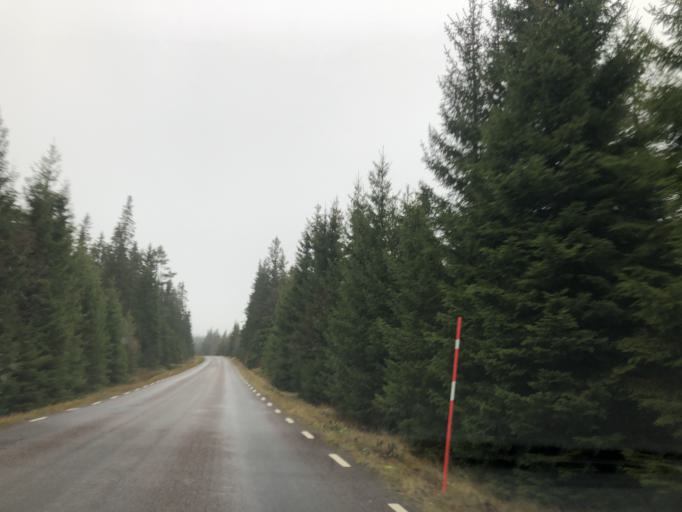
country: SE
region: Vaestra Goetaland
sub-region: Ulricehamns Kommun
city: Ulricehamn
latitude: 57.7372
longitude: 13.5410
